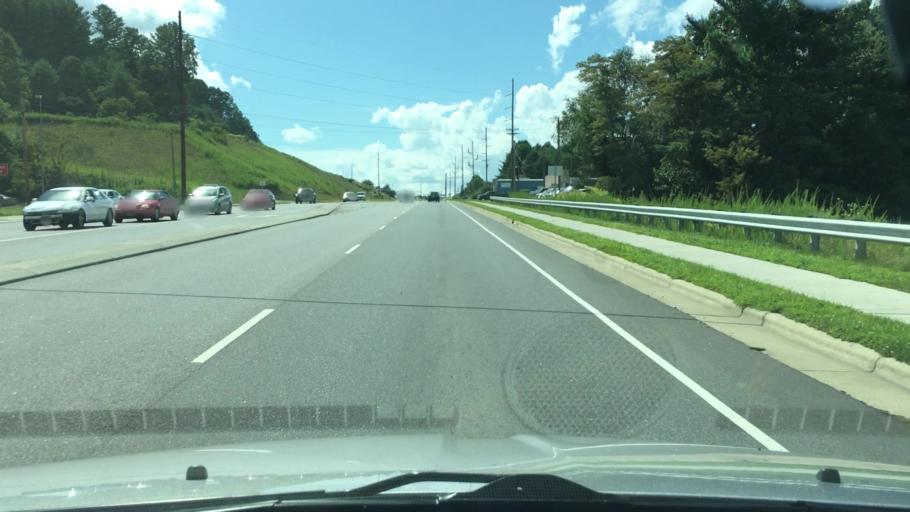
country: US
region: North Carolina
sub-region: Yancey County
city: Burnsville
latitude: 35.9151
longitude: -82.2910
